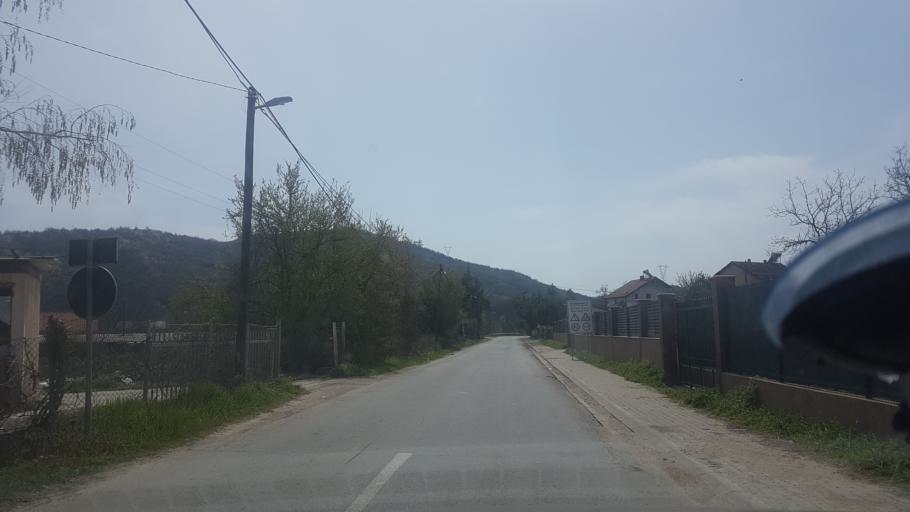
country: MK
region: Zelenikovo
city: Zelenikovo
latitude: 41.8982
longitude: 21.6022
